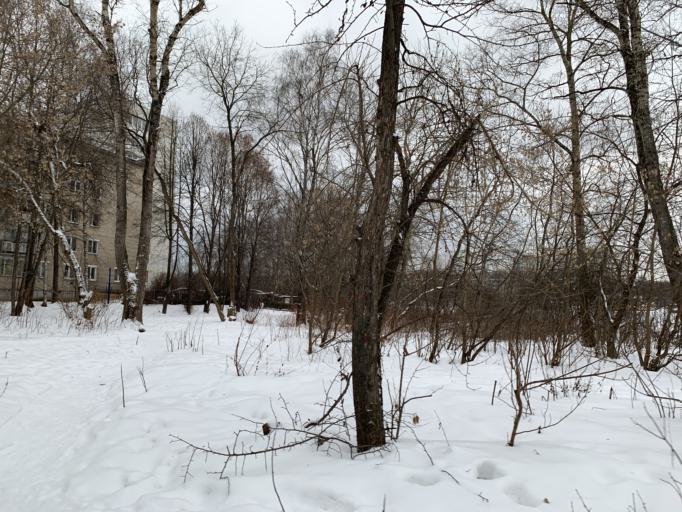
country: RU
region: Moskovskaya
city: Pushkino
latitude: 56.0017
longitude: 37.8660
